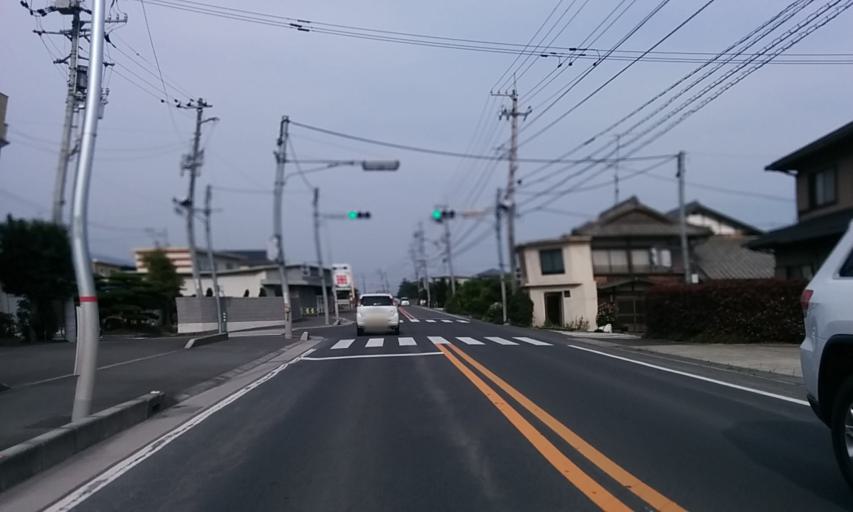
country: JP
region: Ehime
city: Kawanoecho
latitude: 33.9671
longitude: 133.5005
